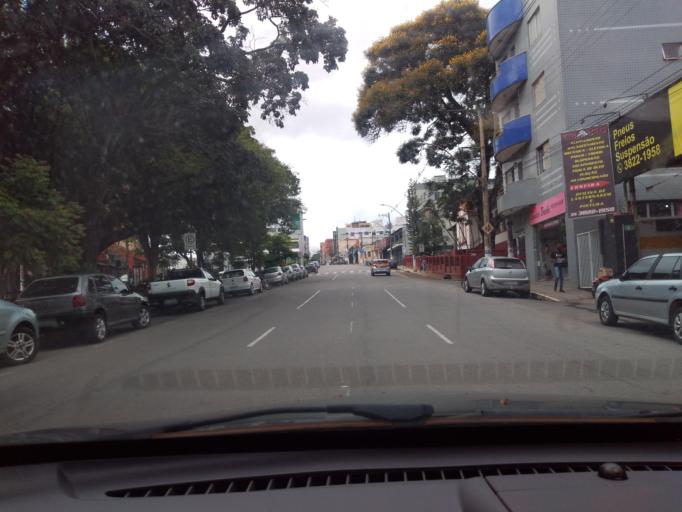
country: BR
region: Minas Gerais
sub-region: Lavras
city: Lavras
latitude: -21.2329
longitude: -44.9977
